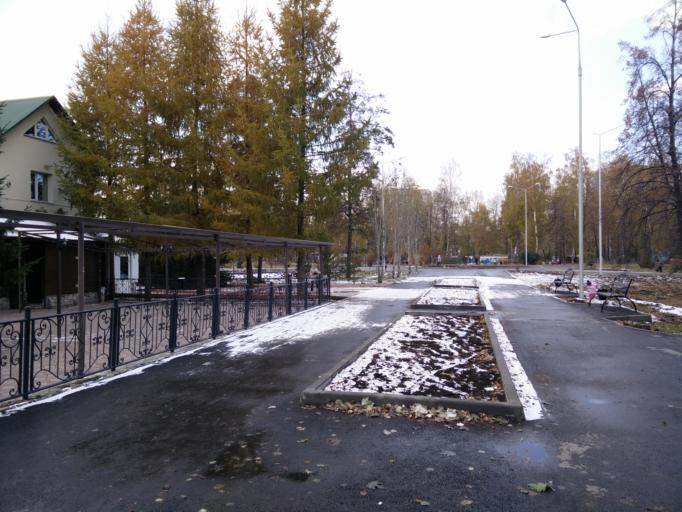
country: RU
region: Novosibirsk
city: Berdsk
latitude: 54.7572
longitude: 83.1040
